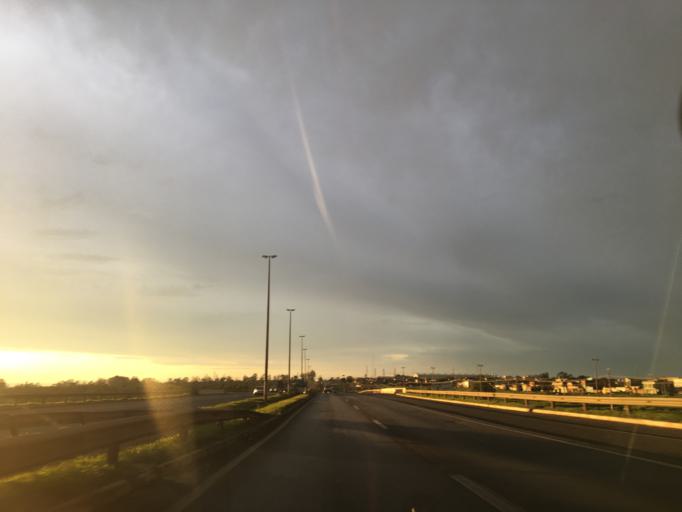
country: BR
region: Federal District
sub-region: Brasilia
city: Brasilia
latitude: -16.0023
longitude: -47.9843
